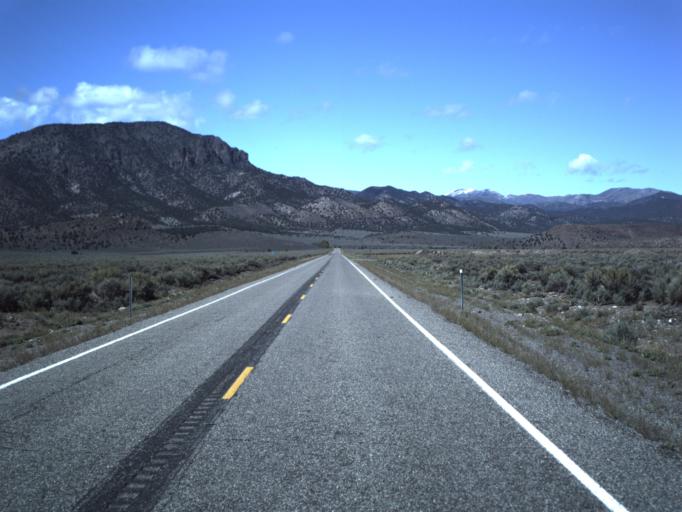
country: US
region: Utah
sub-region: Piute County
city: Junction
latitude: 38.2493
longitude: -112.2379
